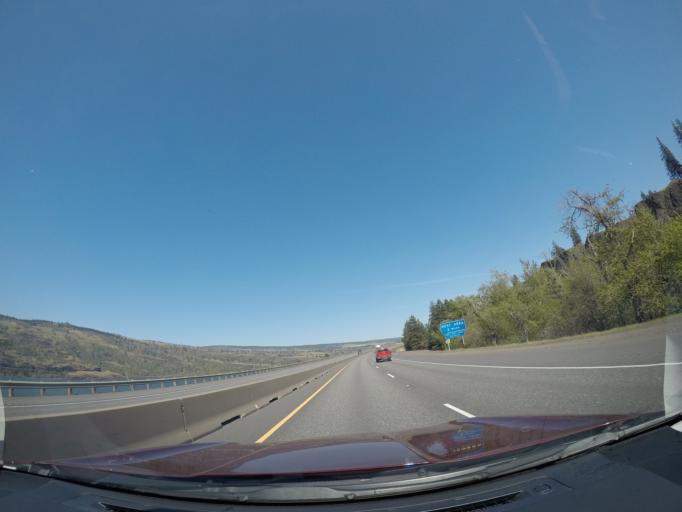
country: US
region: Washington
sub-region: Klickitat County
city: White Salmon
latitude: 45.6927
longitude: -121.3832
